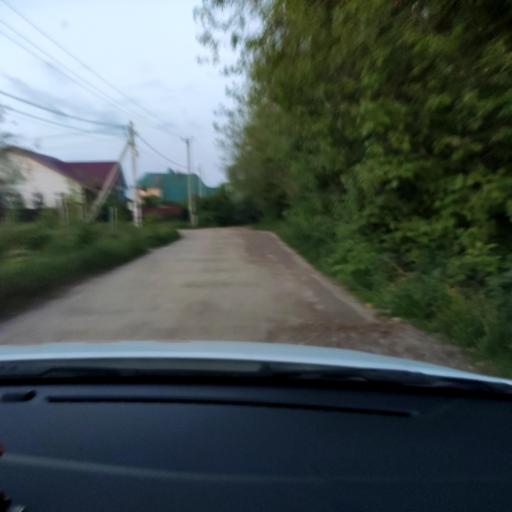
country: RU
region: Tatarstan
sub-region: Gorod Kazan'
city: Kazan
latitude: 55.8806
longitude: 49.1012
